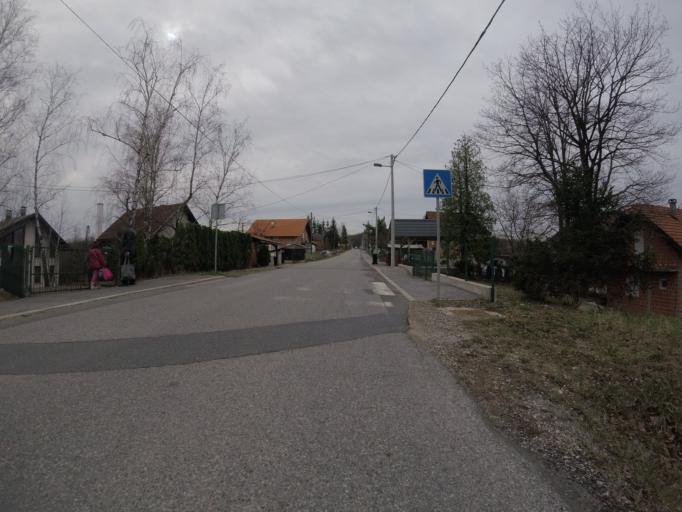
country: HR
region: Grad Zagreb
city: Strmec
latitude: 45.6410
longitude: 15.9352
